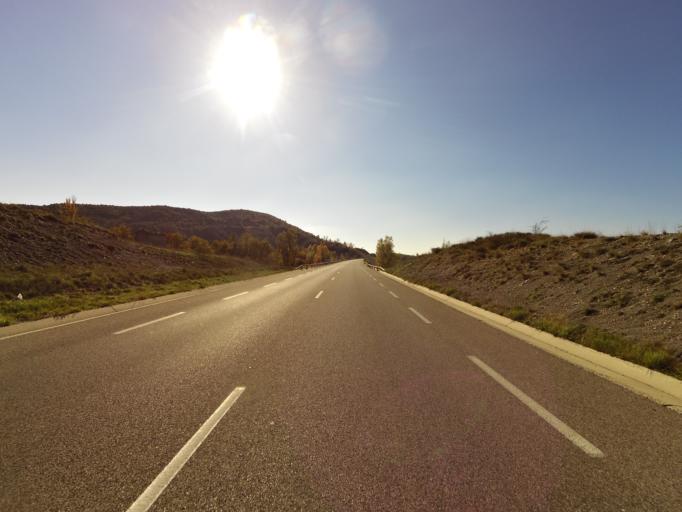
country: FR
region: Rhone-Alpes
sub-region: Departement de l'Ardeche
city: Lachapelle-sous-Aubenas
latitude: 44.5641
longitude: 4.3706
